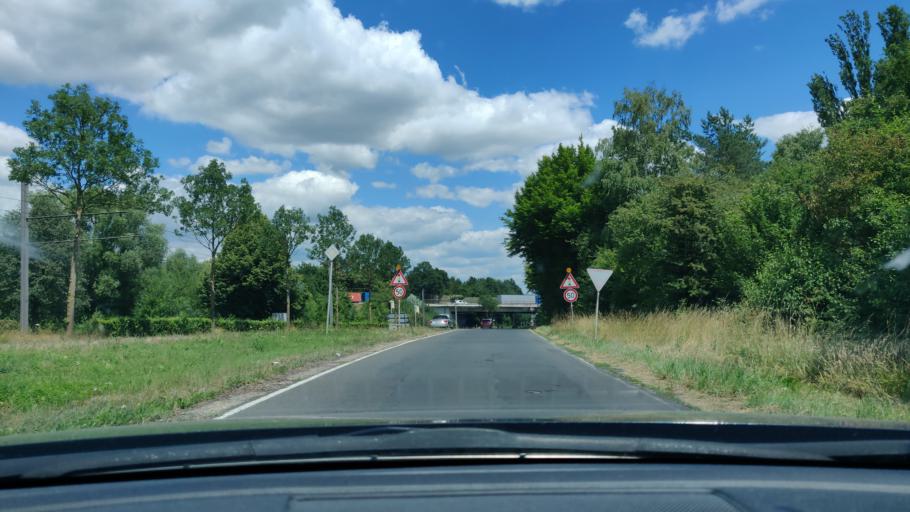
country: DE
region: Hesse
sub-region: Regierungsbezirk Kassel
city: Baunatal
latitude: 51.2658
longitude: 9.4319
